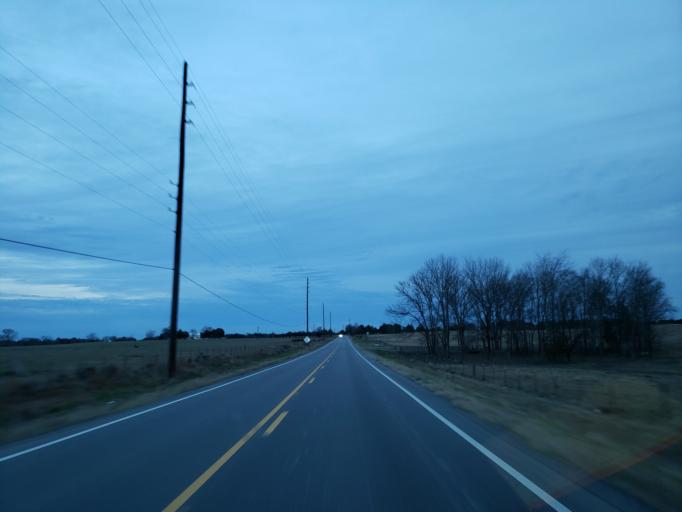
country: US
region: Alabama
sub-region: Sumter County
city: Livingston
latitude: 32.8125
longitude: -88.2772
